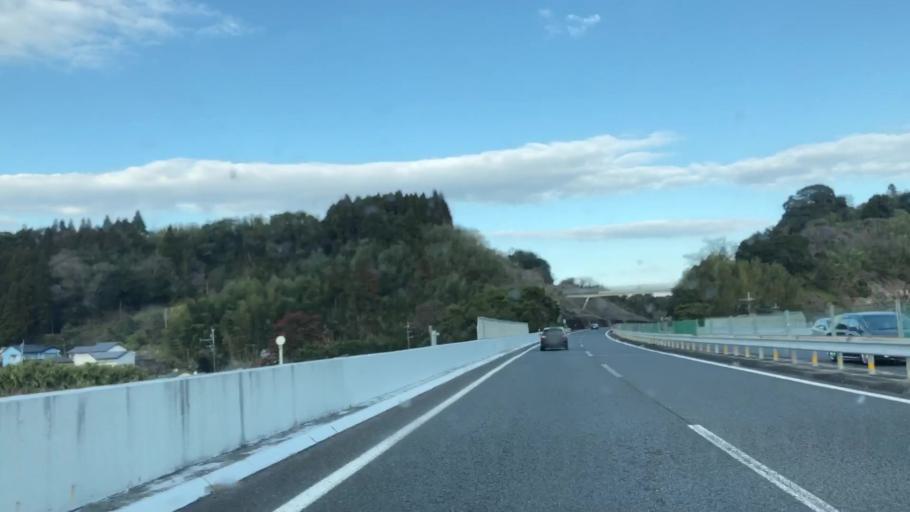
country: JP
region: Miyazaki
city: Miyazaki-shi
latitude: 31.8631
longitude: 131.3819
